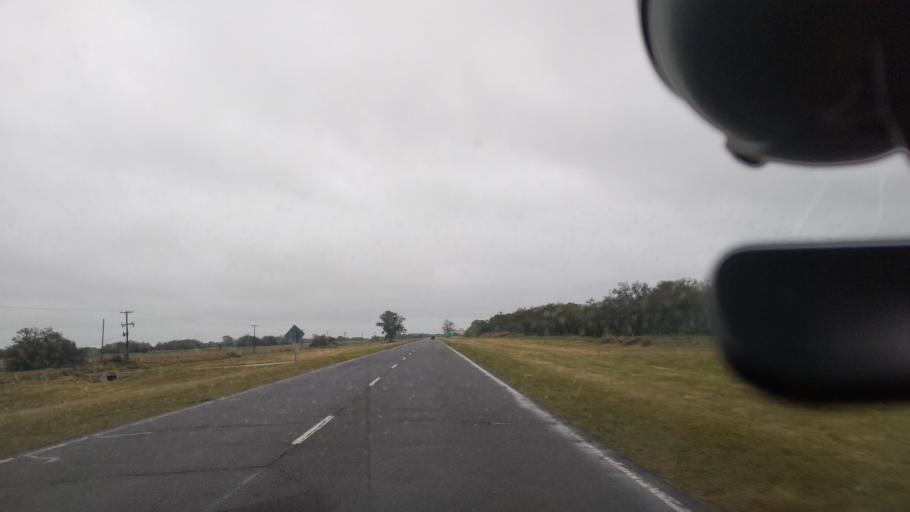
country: AR
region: Buenos Aires
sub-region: Partido de Castelli
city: Castelli
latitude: -36.0358
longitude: -57.4467
